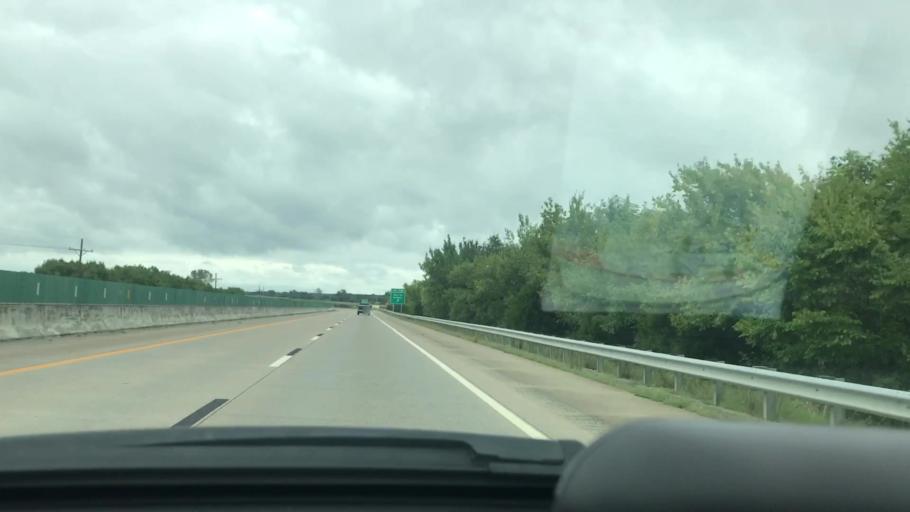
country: US
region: Oklahoma
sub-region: McIntosh County
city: Eufaula
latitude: 35.1258
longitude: -95.6771
